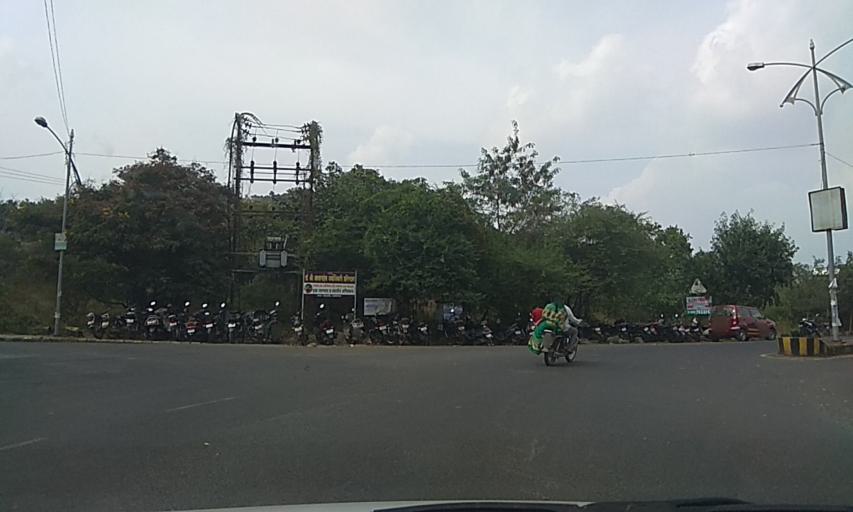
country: IN
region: Maharashtra
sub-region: Pune Division
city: Pimpri
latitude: 18.5977
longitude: 73.7171
